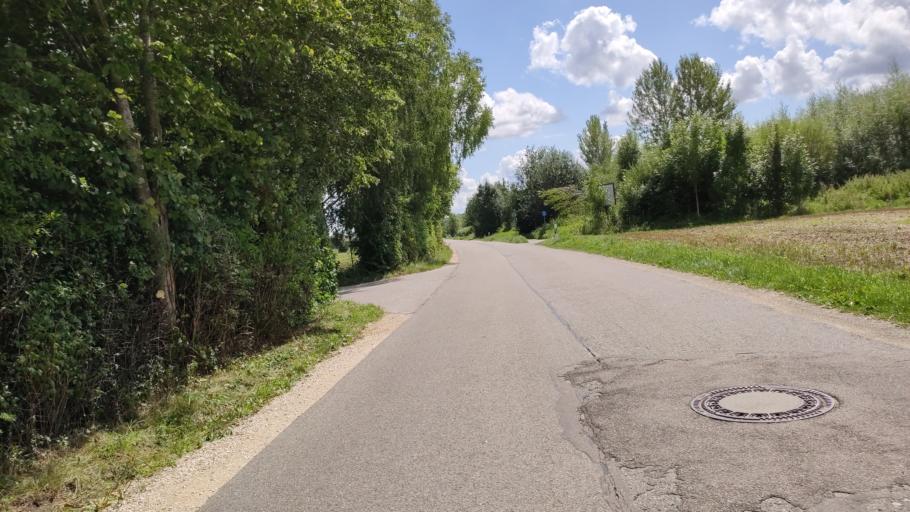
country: DE
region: Bavaria
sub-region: Swabia
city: Konigsbrunn
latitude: 48.2484
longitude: 10.8925
